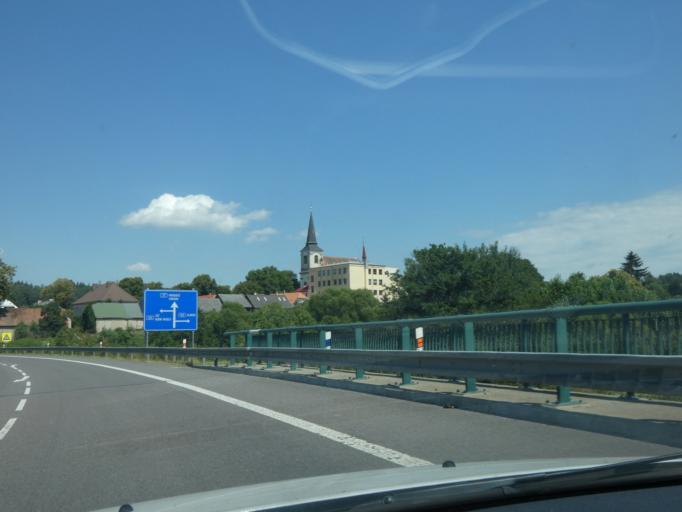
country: CZ
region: Pardubicky
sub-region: Okres Chrudim
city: Nasavrky
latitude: 49.7843
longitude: 15.8163
